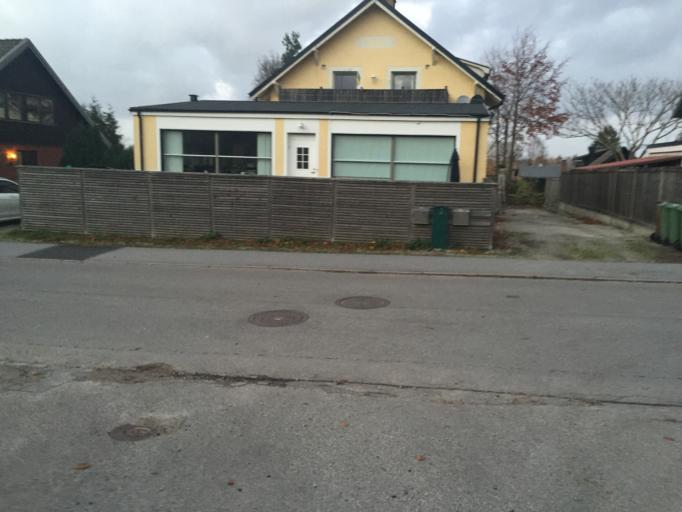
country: SE
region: Skane
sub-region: Staffanstorps Kommun
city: Hjaerup
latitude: 55.6527
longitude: 13.1138
